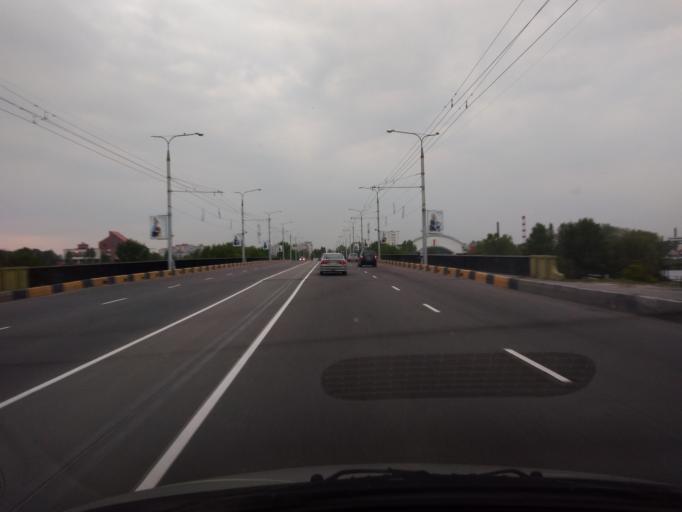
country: BY
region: Brest
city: Brest
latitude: 52.0862
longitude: 23.7352
